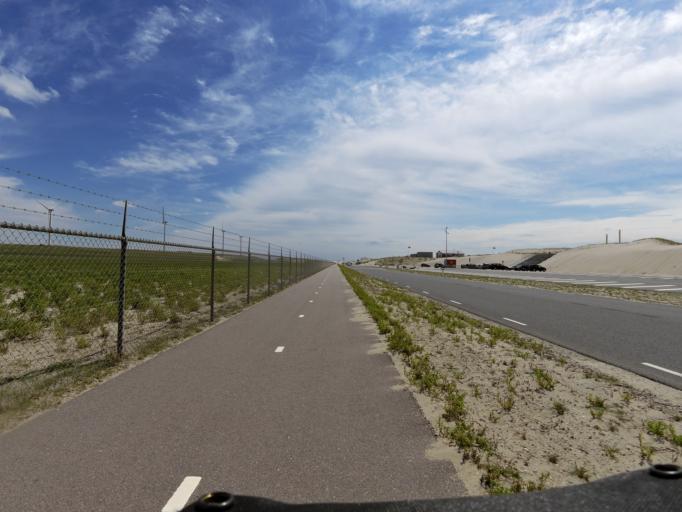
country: NL
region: South Holland
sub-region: Gemeente Goeree-Overflakkee
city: Goedereede
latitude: 51.9287
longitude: 3.9819
